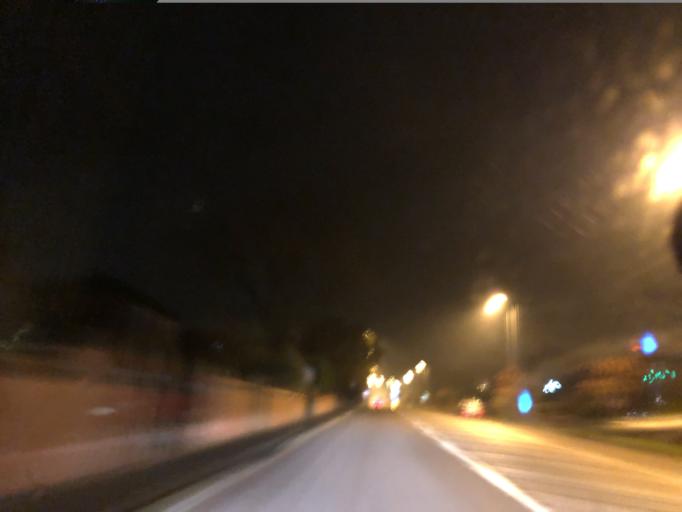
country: GB
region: England
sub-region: Borough of Oldham
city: Shaw
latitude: 53.5669
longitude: -2.0713
